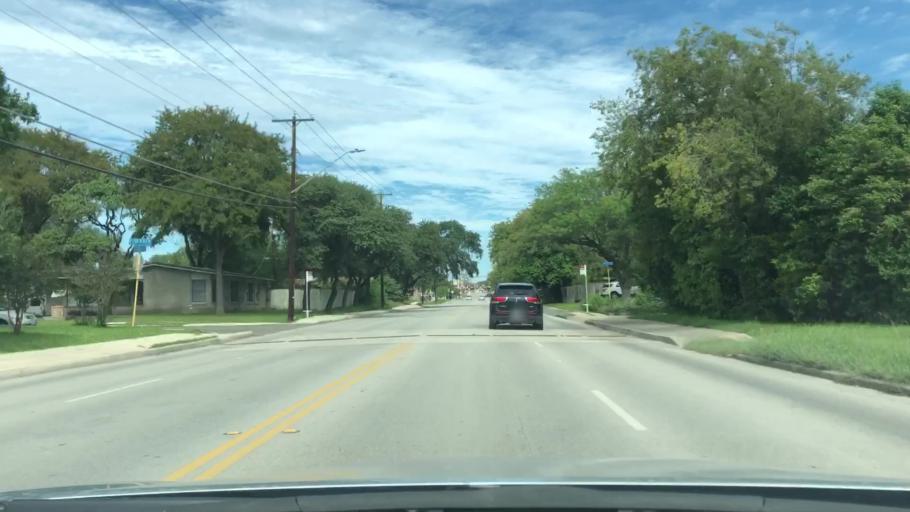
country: US
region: Texas
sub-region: Bexar County
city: Castle Hills
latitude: 29.5097
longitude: -98.4917
